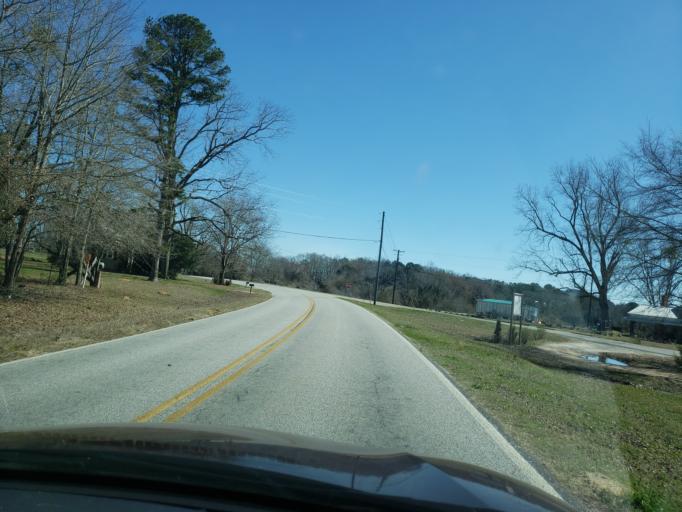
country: US
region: Alabama
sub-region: Elmore County
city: Tallassee
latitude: 32.5816
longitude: -85.7895
